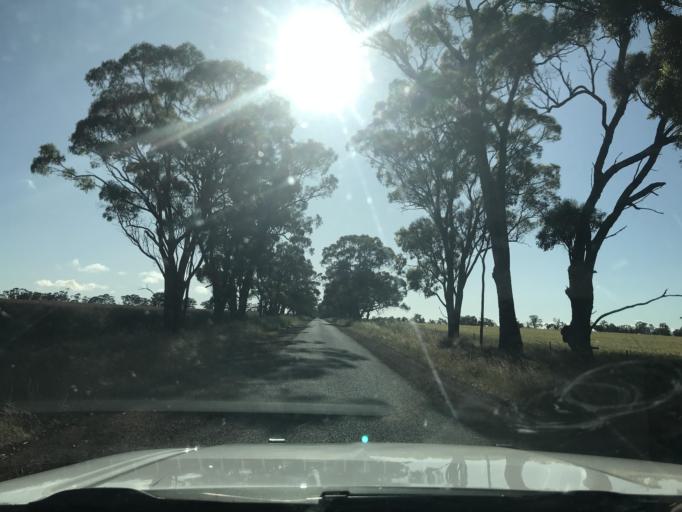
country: AU
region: Victoria
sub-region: Horsham
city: Horsham
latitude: -36.6908
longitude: 141.5319
